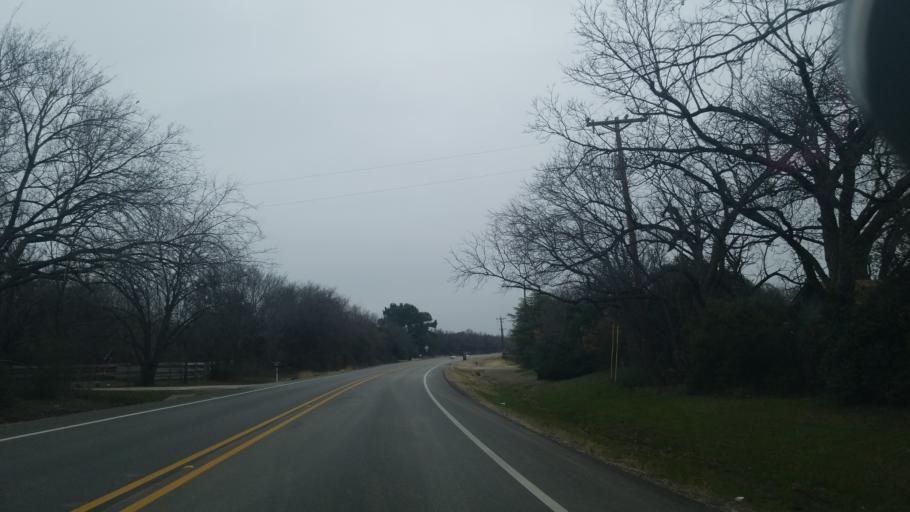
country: US
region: Texas
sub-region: Denton County
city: Argyle
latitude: 33.1379
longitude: -97.1488
